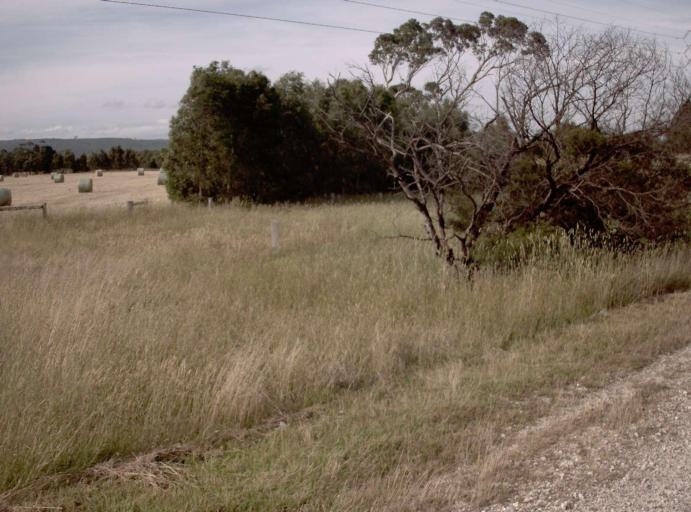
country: AU
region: Victoria
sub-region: Latrobe
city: Traralgon
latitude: -38.1103
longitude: 146.5865
